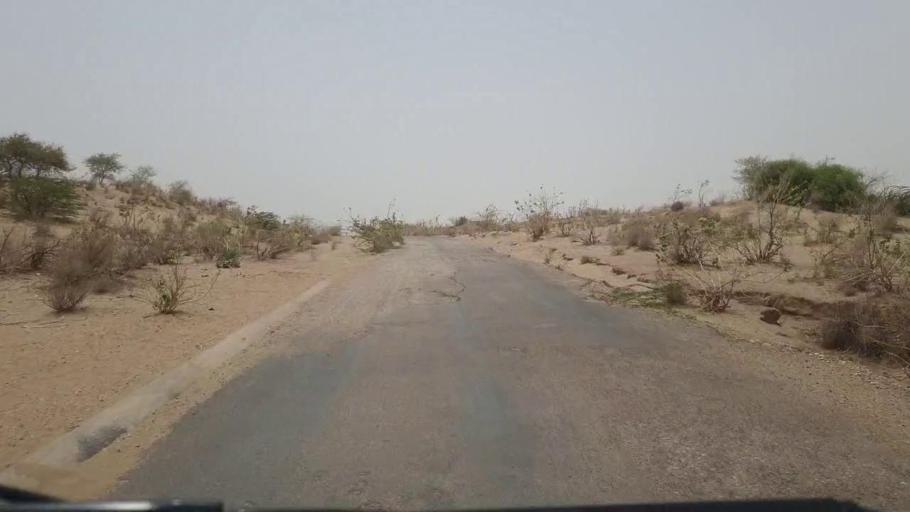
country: PK
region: Sindh
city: Naukot
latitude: 24.7790
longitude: 69.5361
